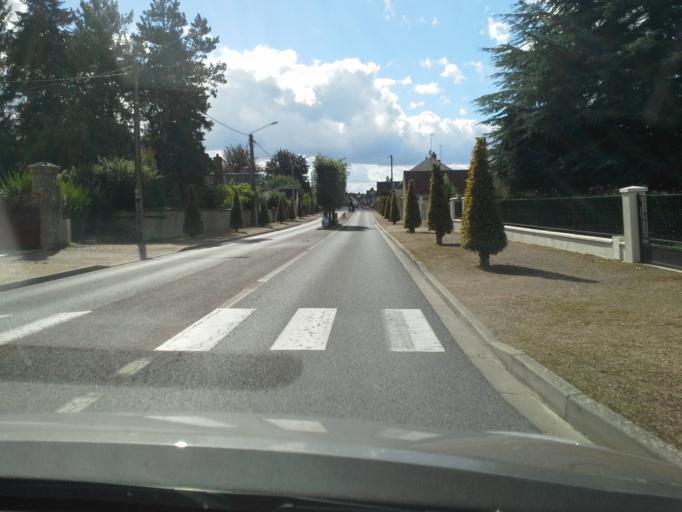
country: FR
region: Centre
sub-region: Departement du Loir-et-Cher
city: Pontlevoy
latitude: 47.3952
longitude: 1.2587
